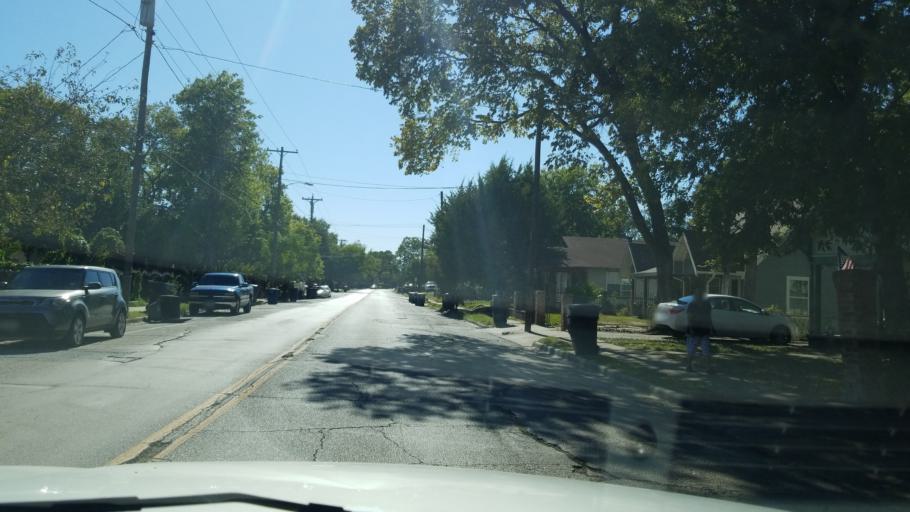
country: US
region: Texas
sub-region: Dallas County
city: Highland Park
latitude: 32.7954
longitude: -96.7520
